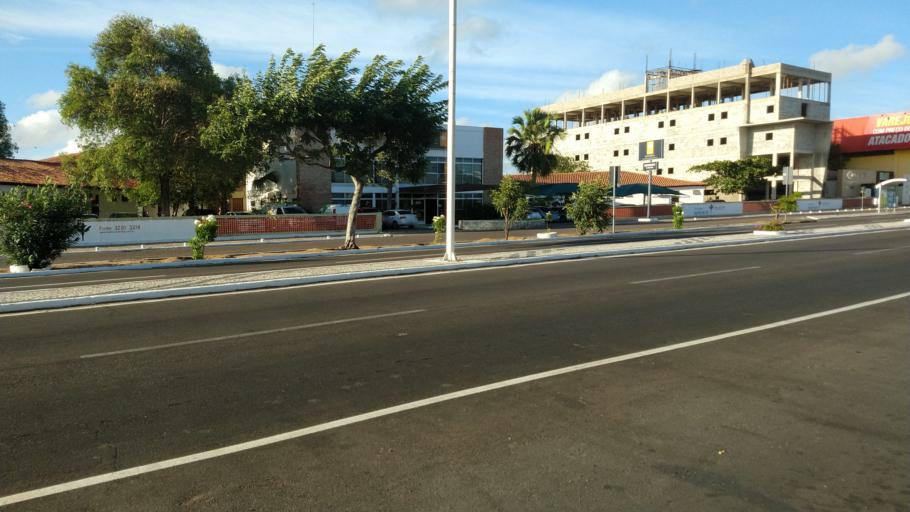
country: BR
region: Bahia
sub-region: Paulo Afonso
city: Paulo Afonso
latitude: -9.3982
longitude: -38.2223
